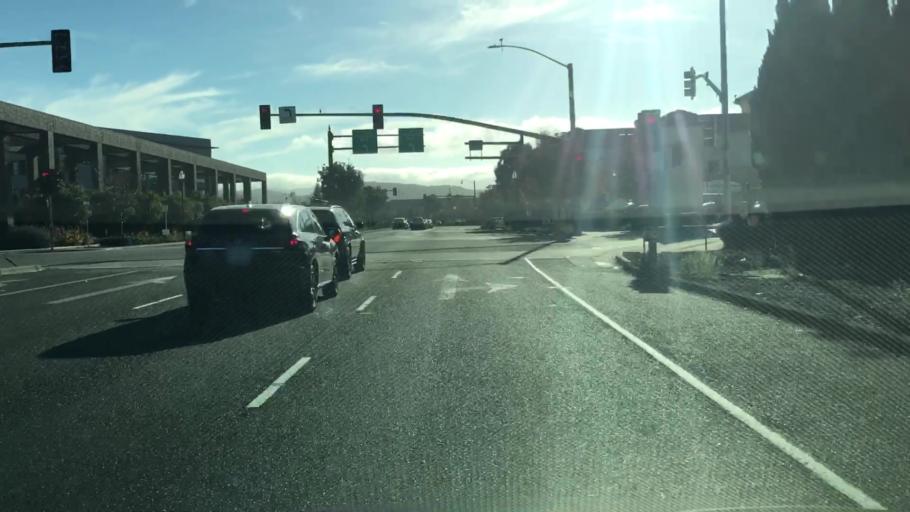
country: US
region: California
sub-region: San Mateo County
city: Foster City
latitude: 37.5444
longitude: -122.2904
